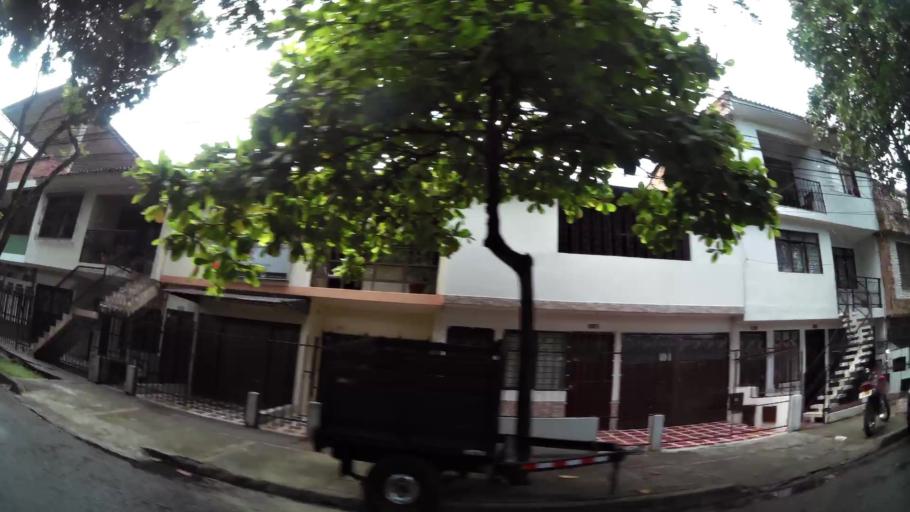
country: CO
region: Valle del Cauca
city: Cali
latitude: 3.3891
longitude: -76.5468
